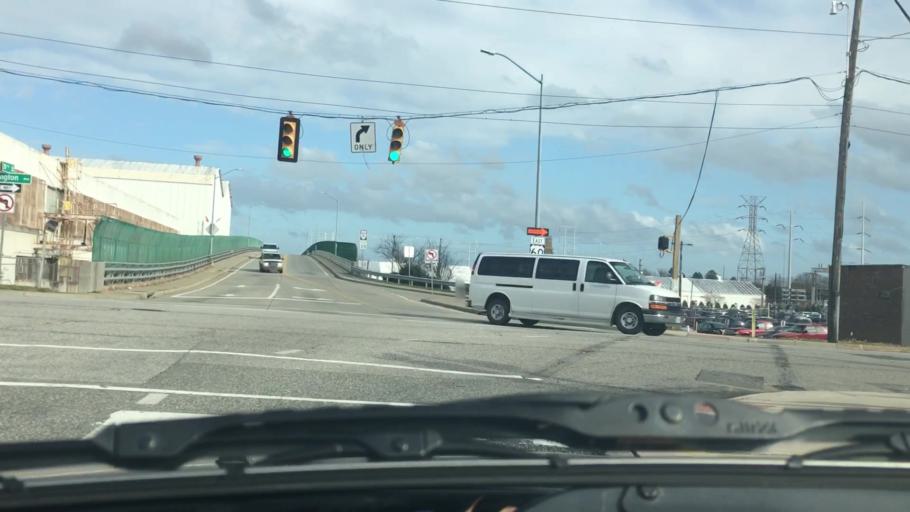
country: US
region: Virginia
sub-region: City of Newport News
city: Newport News
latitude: 36.9873
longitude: -76.4342
